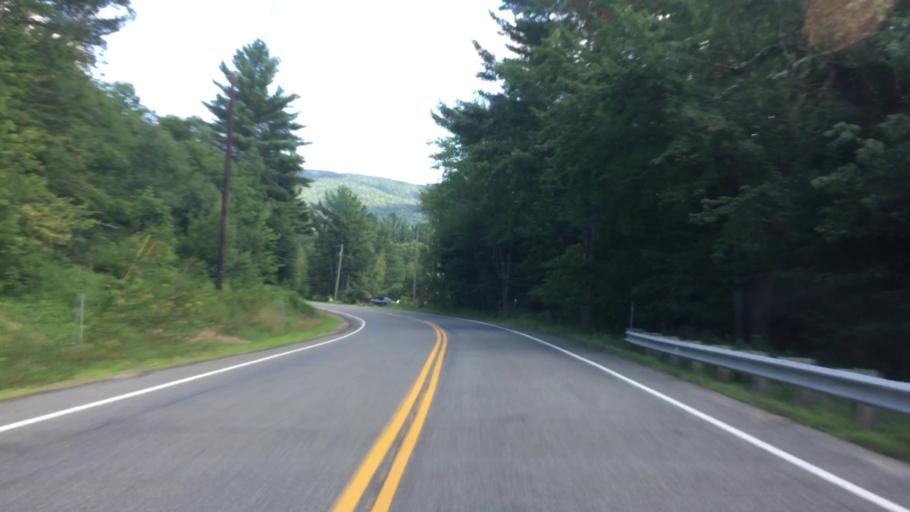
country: US
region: New Hampshire
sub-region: Grafton County
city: Woodstock
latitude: 44.0793
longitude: -71.8027
